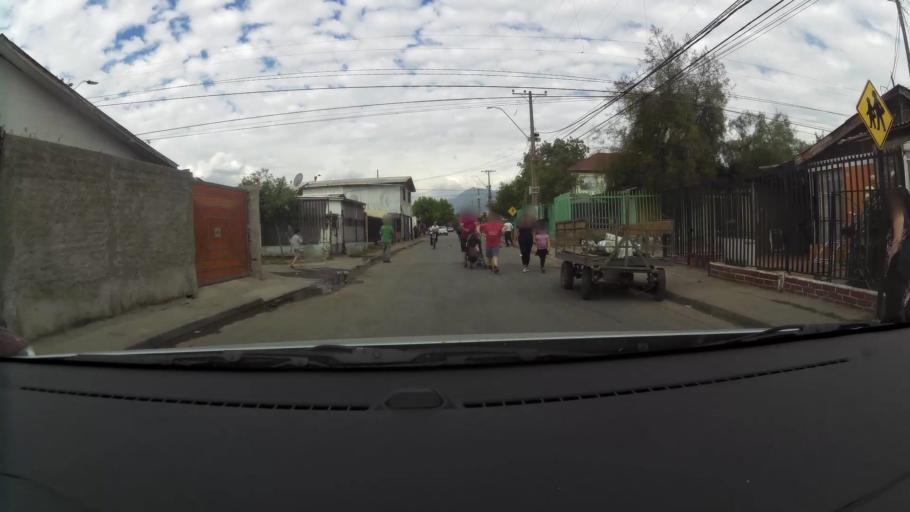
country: CL
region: Santiago Metropolitan
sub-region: Provincia de Santiago
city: La Pintana
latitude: -33.6151
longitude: -70.6251
